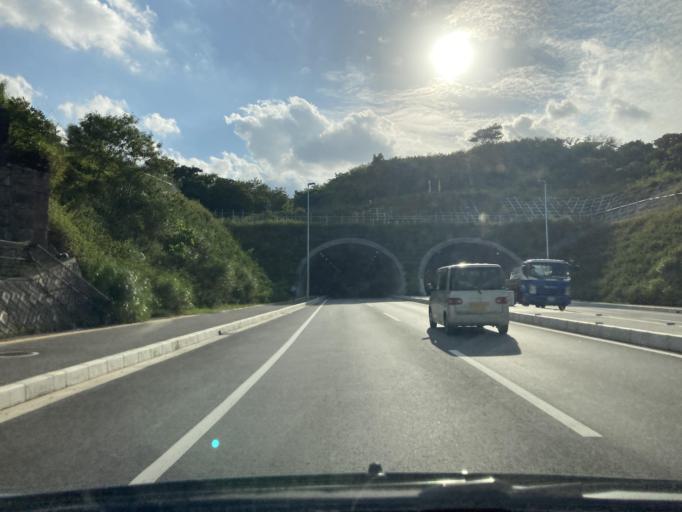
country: JP
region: Okinawa
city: Chatan
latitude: 26.2998
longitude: 127.8035
